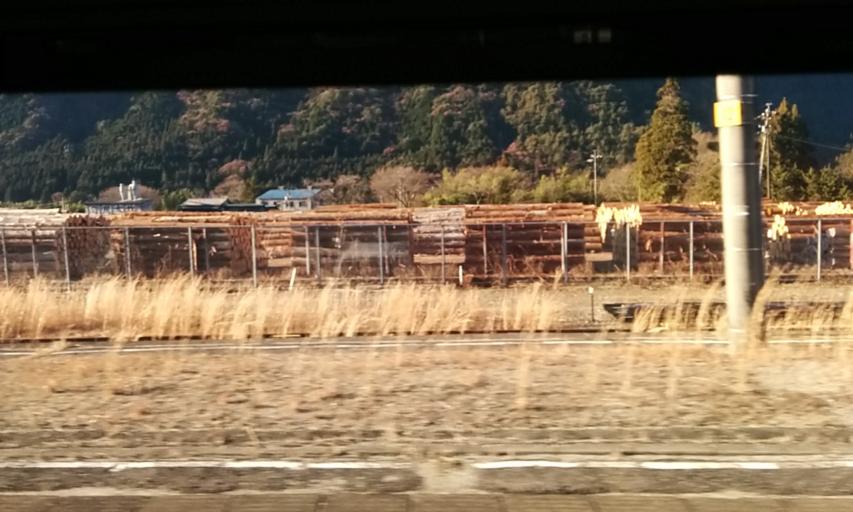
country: JP
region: Gifu
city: Nakatsugawa
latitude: 35.6725
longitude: 137.6354
